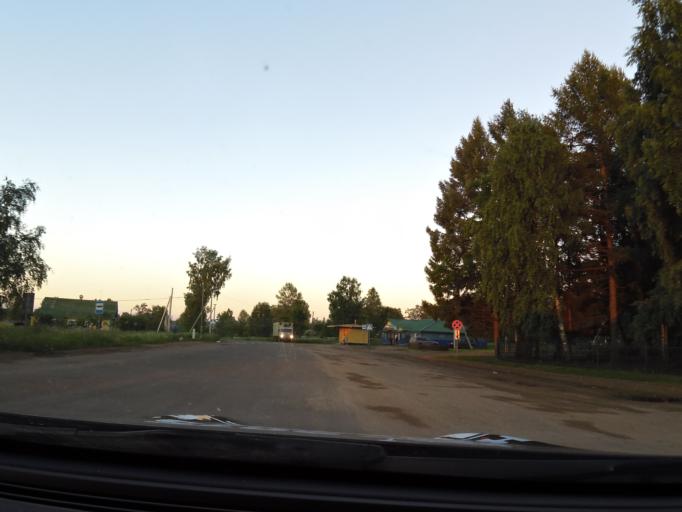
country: RU
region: Leningrad
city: Voznesen'ye
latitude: 60.8508
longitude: 35.5568
